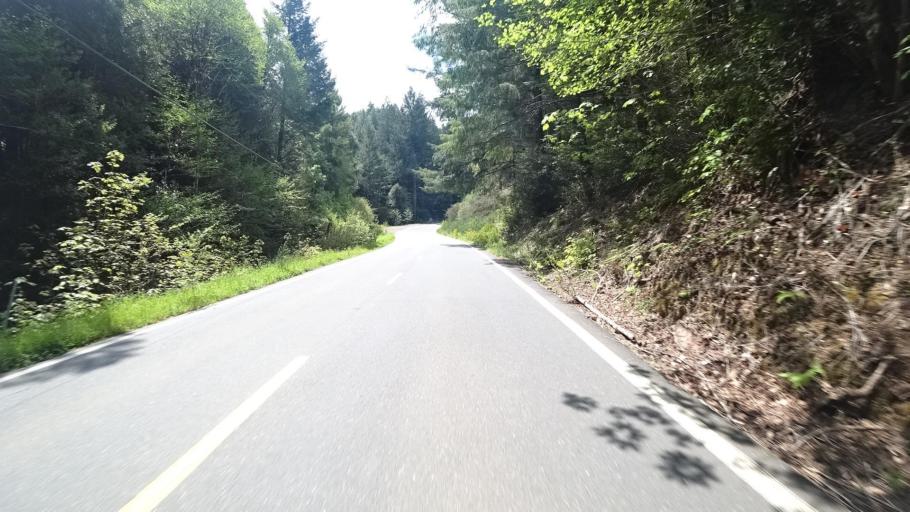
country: US
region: California
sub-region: Humboldt County
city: Redway
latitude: 40.0845
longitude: -123.9484
